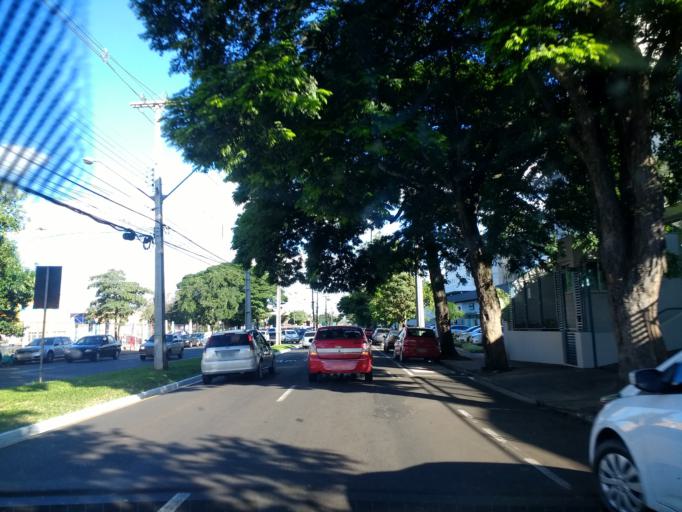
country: BR
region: Parana
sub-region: Londrina
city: Londrina
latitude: -23.3295
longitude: -51.1531
